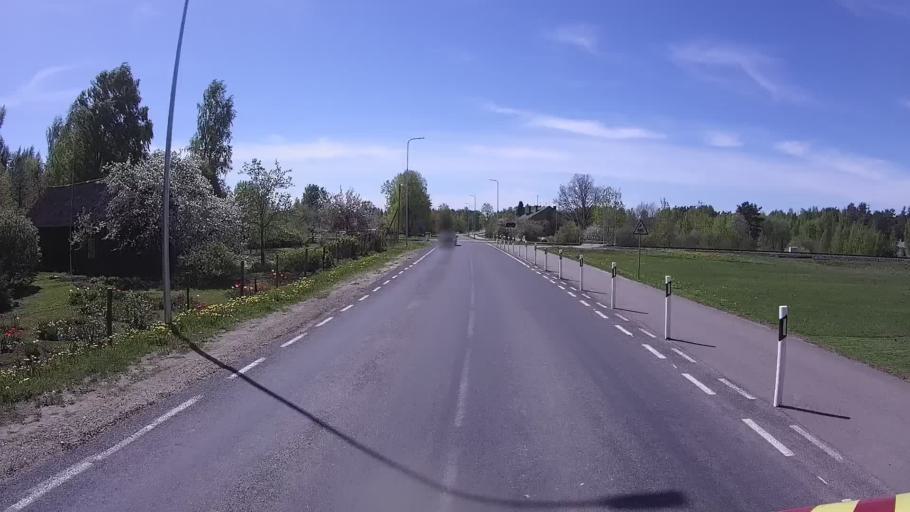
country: EE
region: Polvamaa
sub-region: Raepina vald
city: Rapina
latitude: 58.0089
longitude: 27.3512
